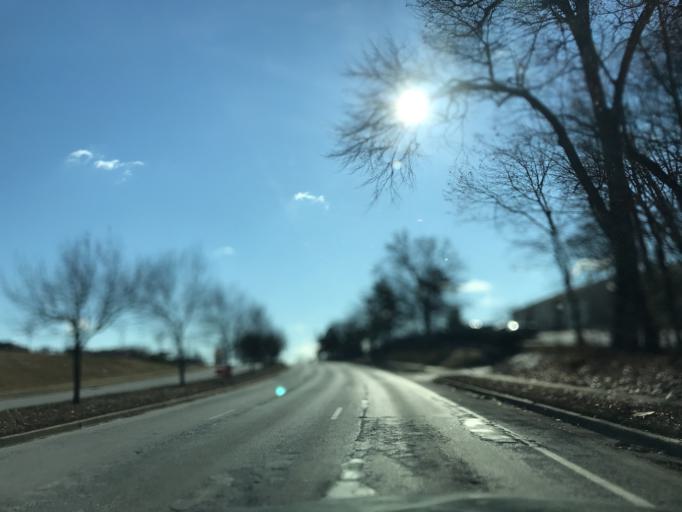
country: US
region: Maryland
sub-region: Baltimore County
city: Towson
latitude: 39.3984
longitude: -76.5867
